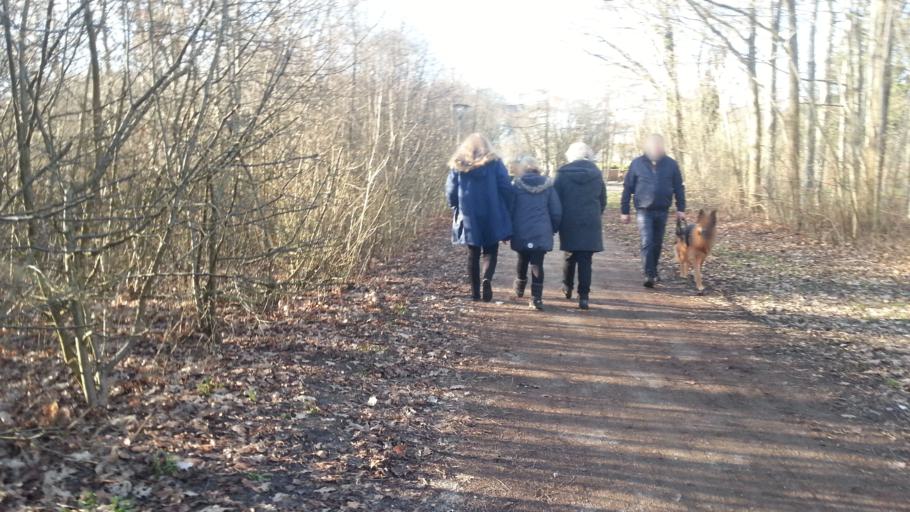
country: DK
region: South Denmark
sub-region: Varde Kommune
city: Varde
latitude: 55.6193
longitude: 8.4883
